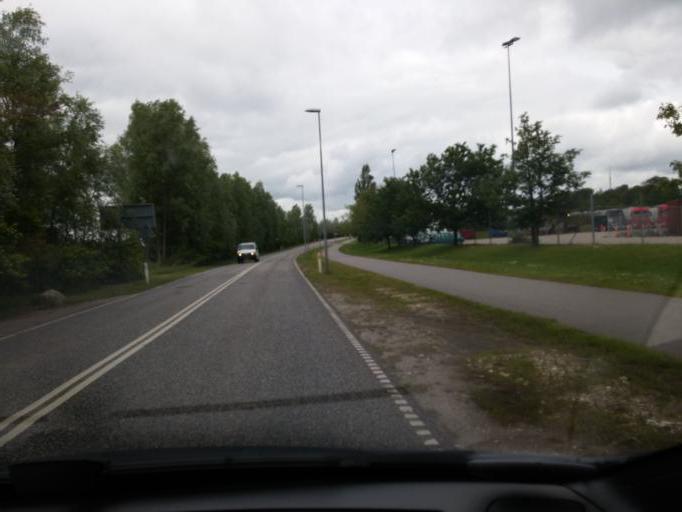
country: DK
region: Capital Region
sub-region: Hillerod Kommune
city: Hillerod
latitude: 55.9196
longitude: 12.2815
